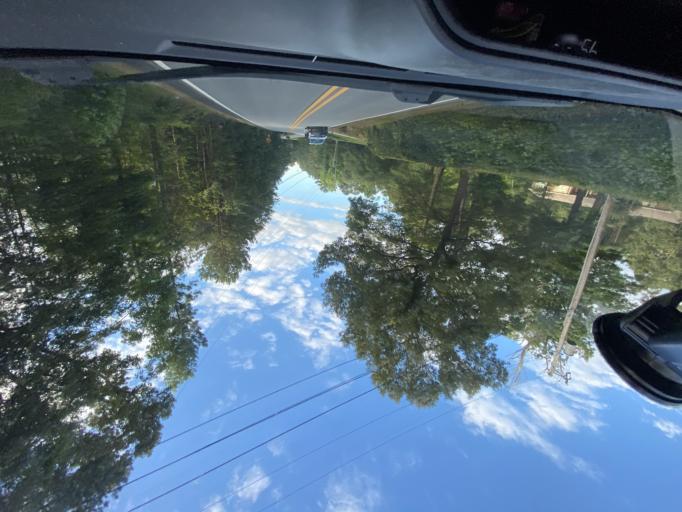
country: US
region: Georgia
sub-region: Fayette County
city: Peachtree City
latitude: 33.4268
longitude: -84.6500
